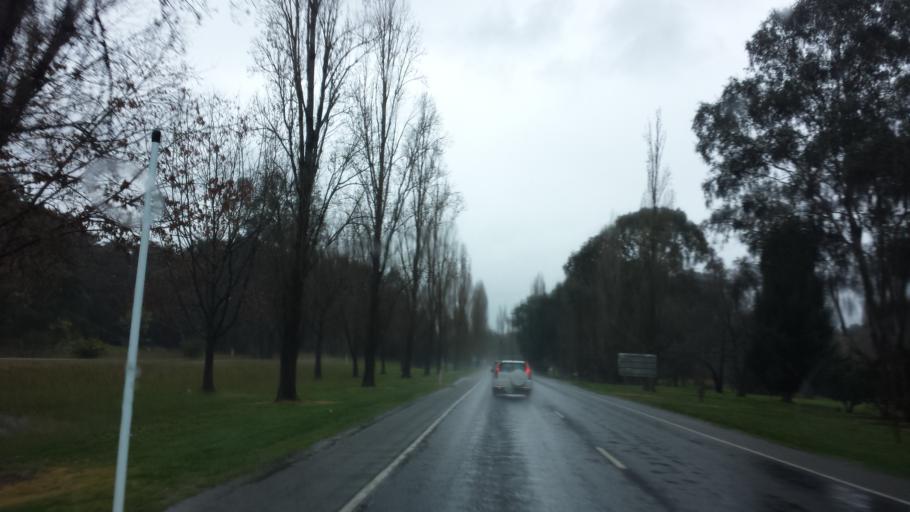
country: AU
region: Victoria
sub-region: Wangaratta
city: Wangaratta
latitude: -36.5528
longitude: 146.7036
